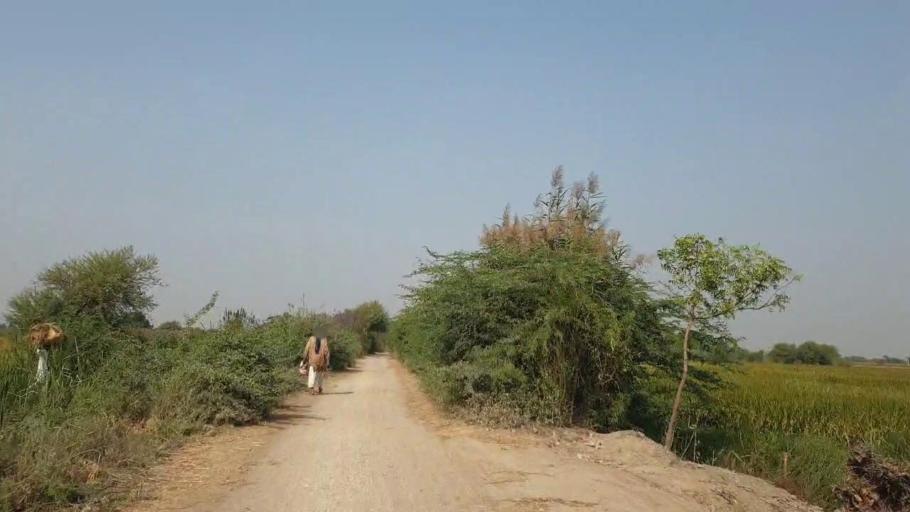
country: PK
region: Sindh
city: Matli
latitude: 24.9495
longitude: 68.5565
